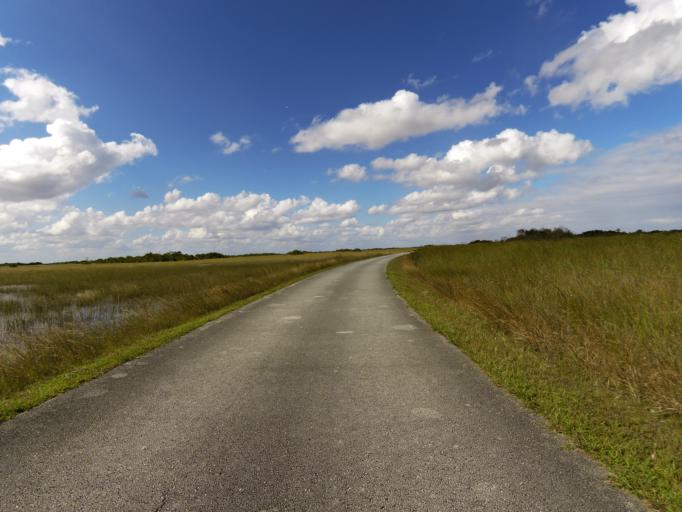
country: US
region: Florida
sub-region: Miami-Dade County
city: The Hammocks
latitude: 25.7284
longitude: -80.7594
